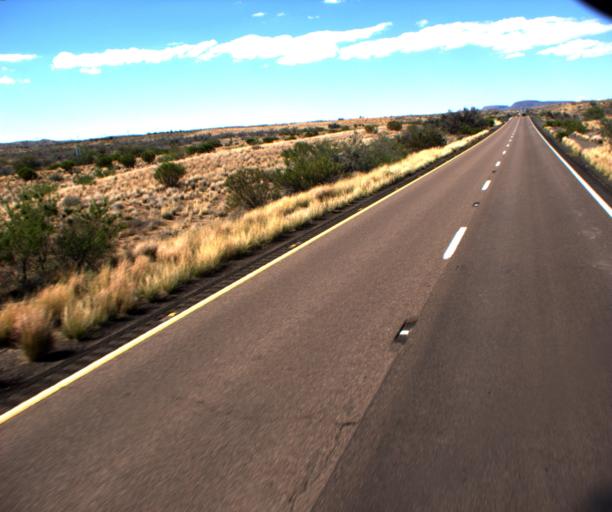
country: US
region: Arizona
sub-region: Mohave County
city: Kingman
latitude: 35.0534
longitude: -113.6648
